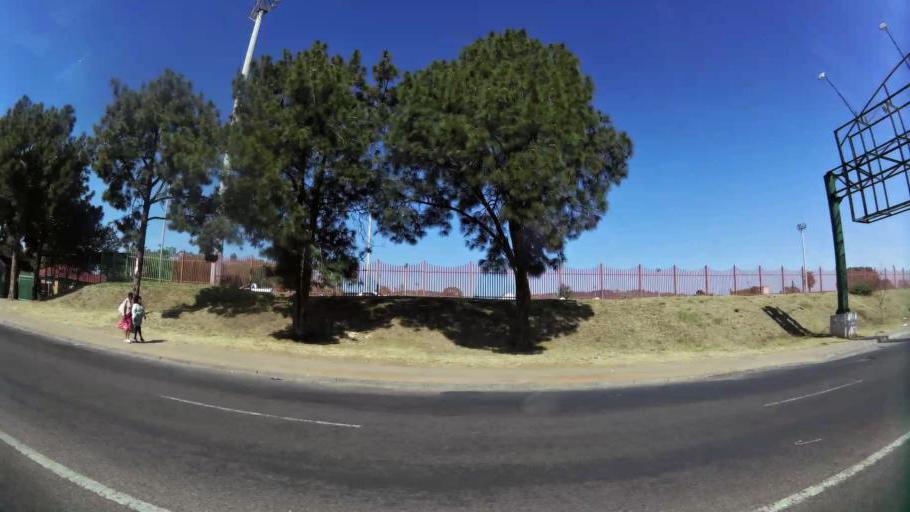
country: ZA
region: Gauteng
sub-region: City of Tshwane Metropolitan Municipality
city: Pretoria
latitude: -25.7476
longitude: 28.1716
